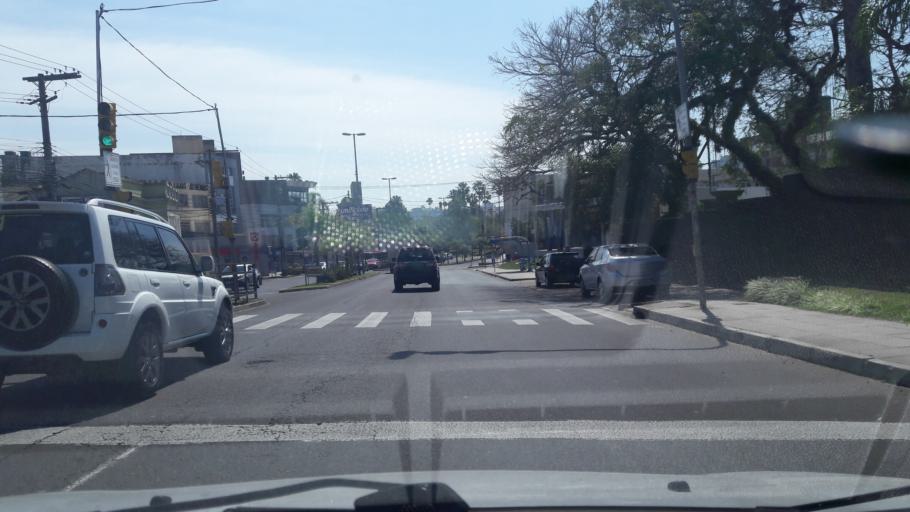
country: BR
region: Rio Grande do Sul
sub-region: Guaiba
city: Guaiba
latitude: -30.1129
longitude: -51.2552
